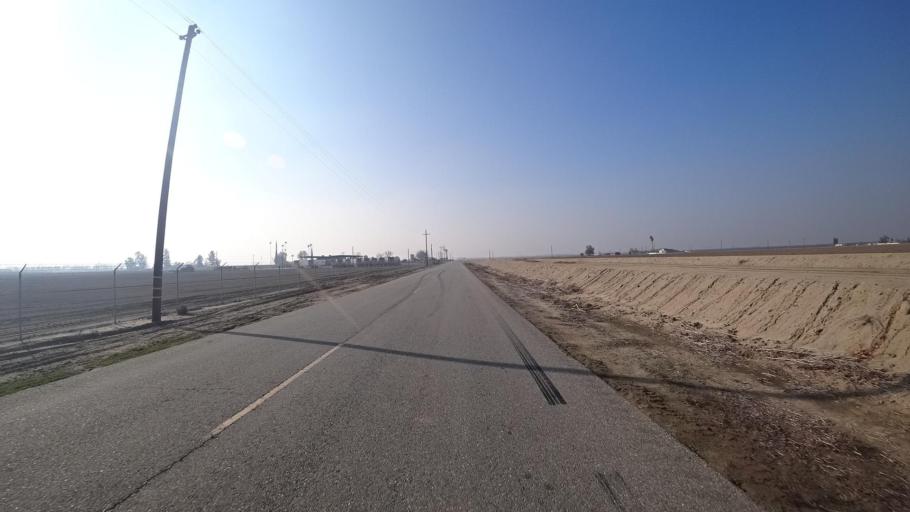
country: US
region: California
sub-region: Kern County
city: Greenfield
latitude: 35.2233
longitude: -119.0352
